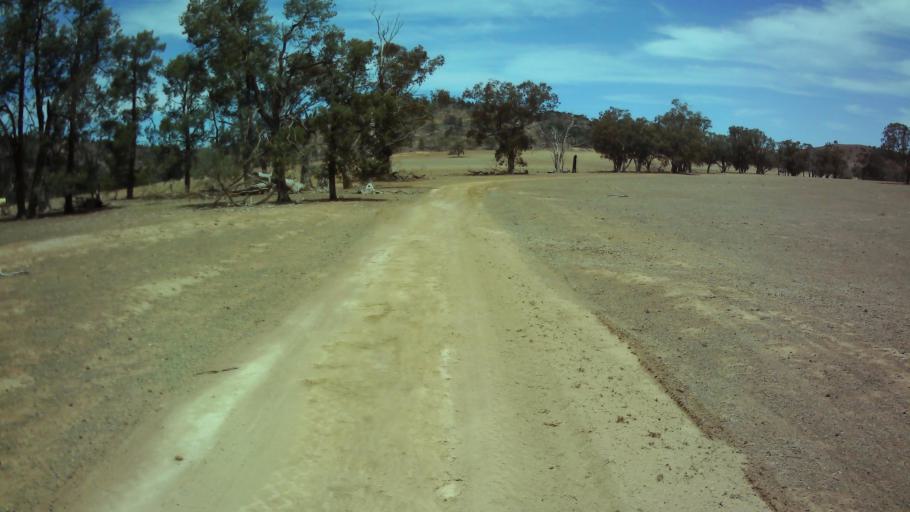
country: AU
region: New South Wales
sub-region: Weddin
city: Grenfell
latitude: -33.7722
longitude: 148.1517
